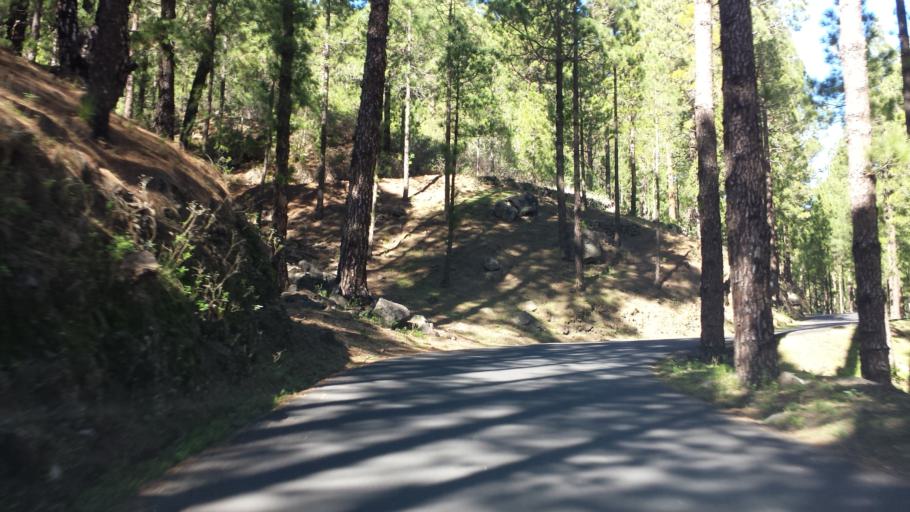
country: ES
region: Canary Islands
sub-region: Provincia de Santa Cruz de Tenerife
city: El Paso
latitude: 28.6911
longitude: -17.8515
